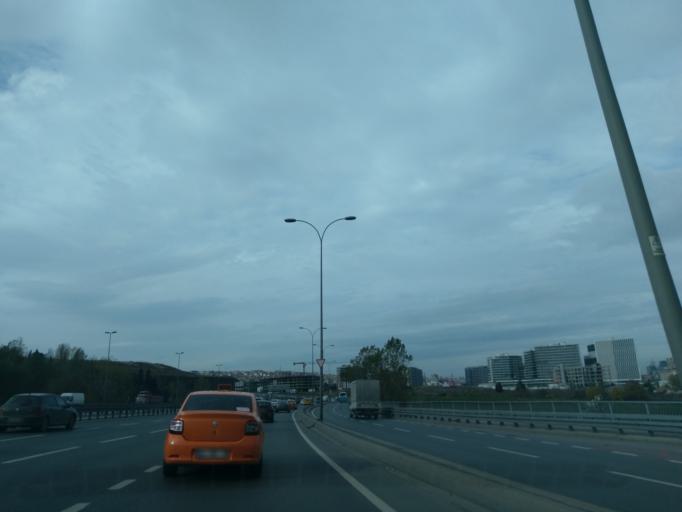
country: TR
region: Istanbul
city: Bahcelievler
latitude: 40.9955
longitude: 28.8151
